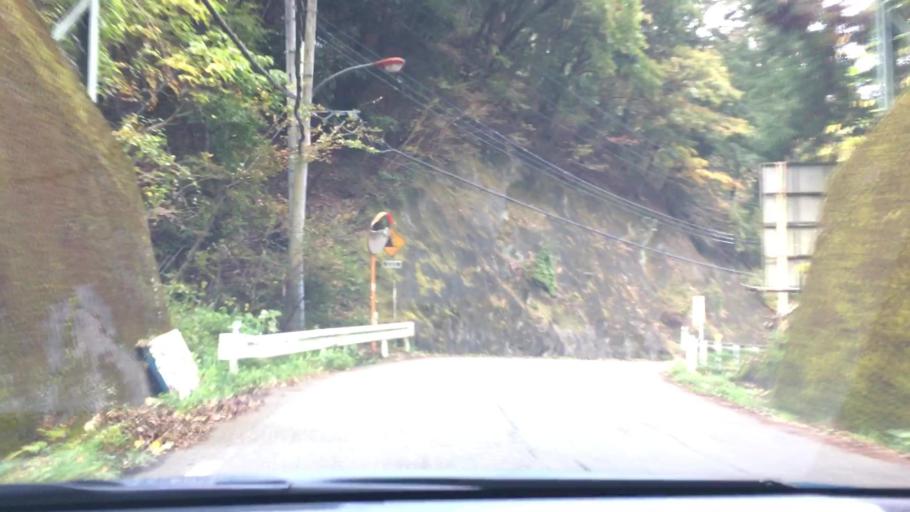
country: JP
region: Yamanashi
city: Uenohara
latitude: 35.5598
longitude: 139.1419
